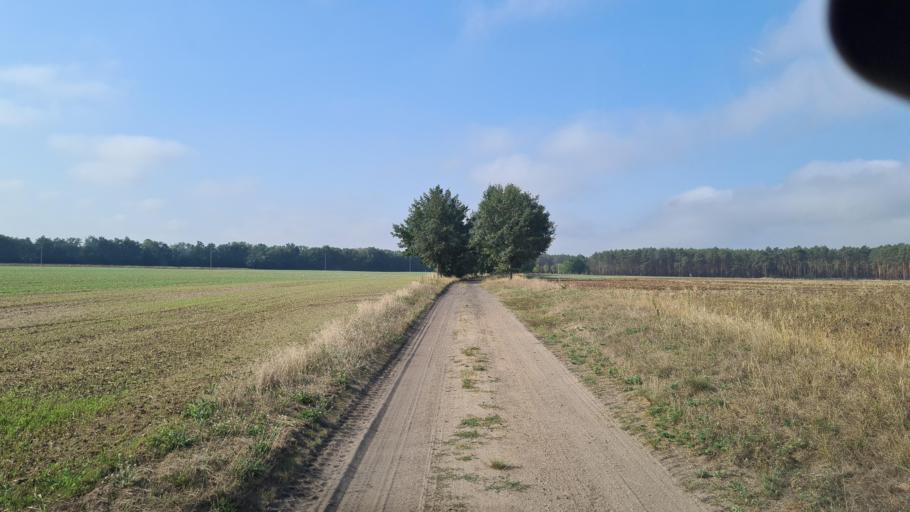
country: DE
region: Brandenburg
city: Belzig
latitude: 52.1664
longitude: 12.6656
